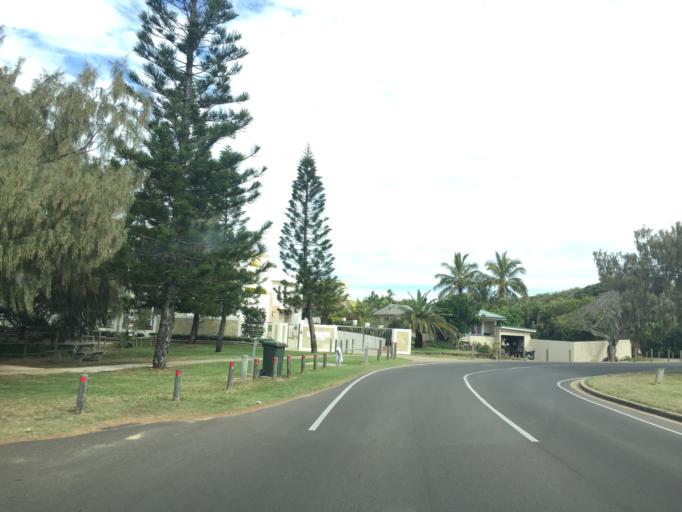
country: AU
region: Queensland
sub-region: Bundaberg
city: Bundaberg
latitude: -24.8290
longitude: 152.4673
